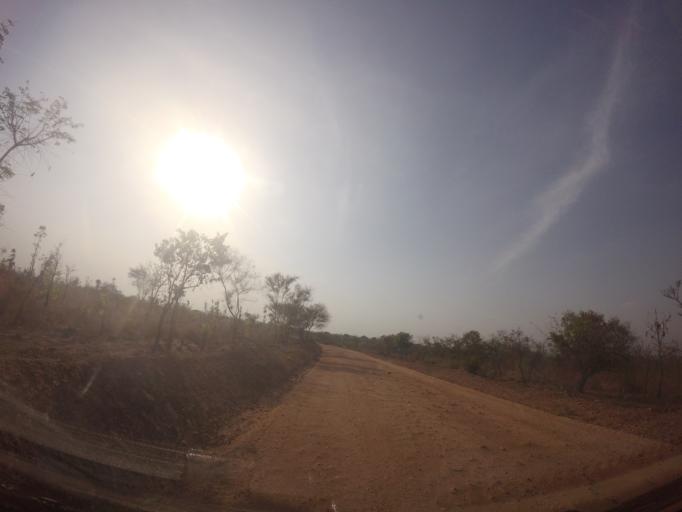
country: UG
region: Northern Region
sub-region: Maracha District
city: Maracha
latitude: 3.1127
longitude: 31.1491
